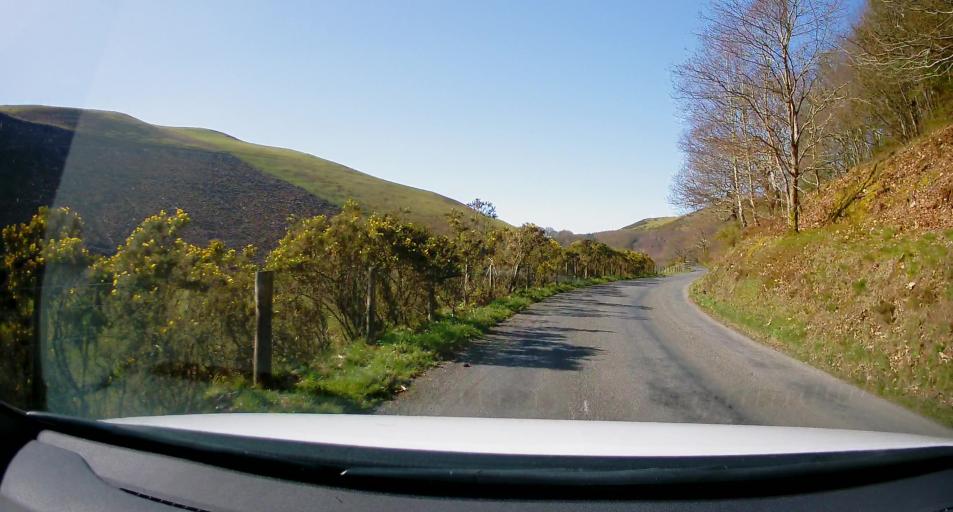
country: GB
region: Wales
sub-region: County of Ceredigion
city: Lledrod
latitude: 52.3513
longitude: -3.9114
